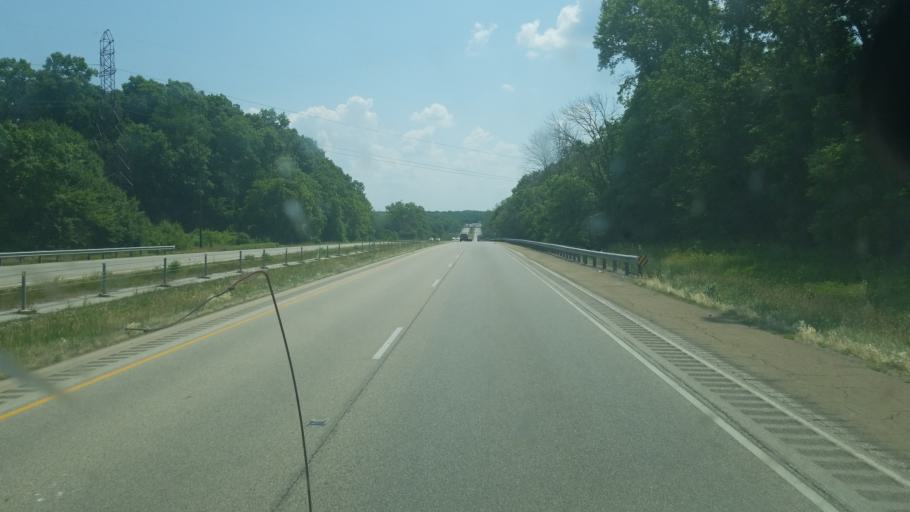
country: US
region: Illinois
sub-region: Vermilion County
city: Oakwood
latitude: 40.1274
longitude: -87.7413
